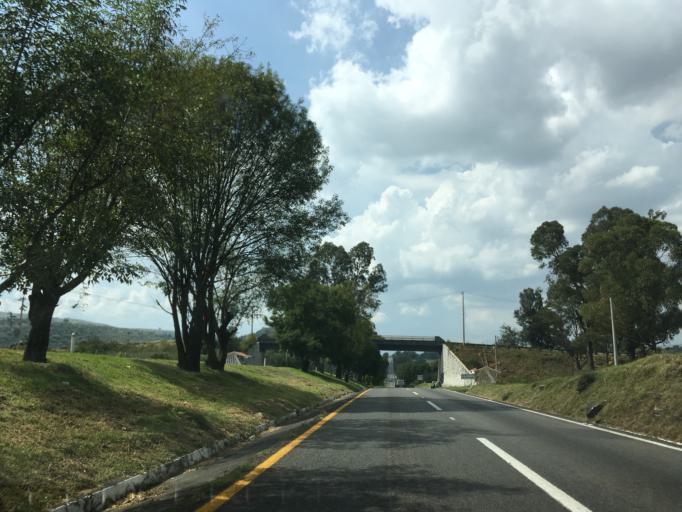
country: MX
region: Michoacan
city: Lagunillas
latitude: 19.5553
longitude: -101.3887
